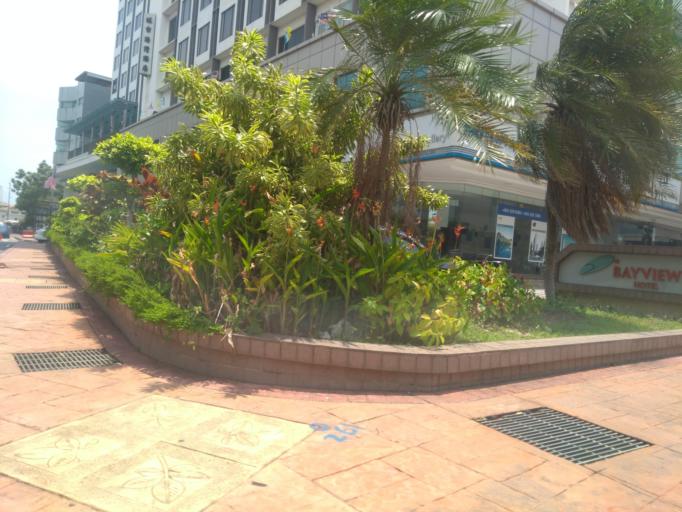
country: MY
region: Penang
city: George Town
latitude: 5.4219
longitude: 100.3364
